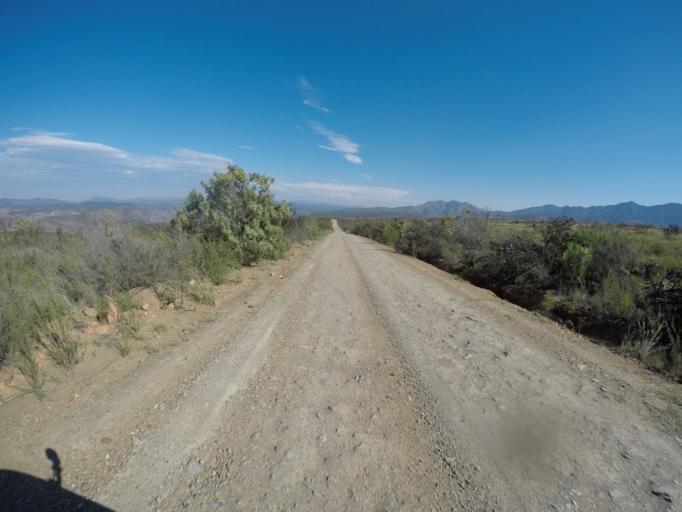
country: ZA
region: Eastern Cape
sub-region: Cacadu District Municipality
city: Kareedouw
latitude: -33.6348
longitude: 24.4727
